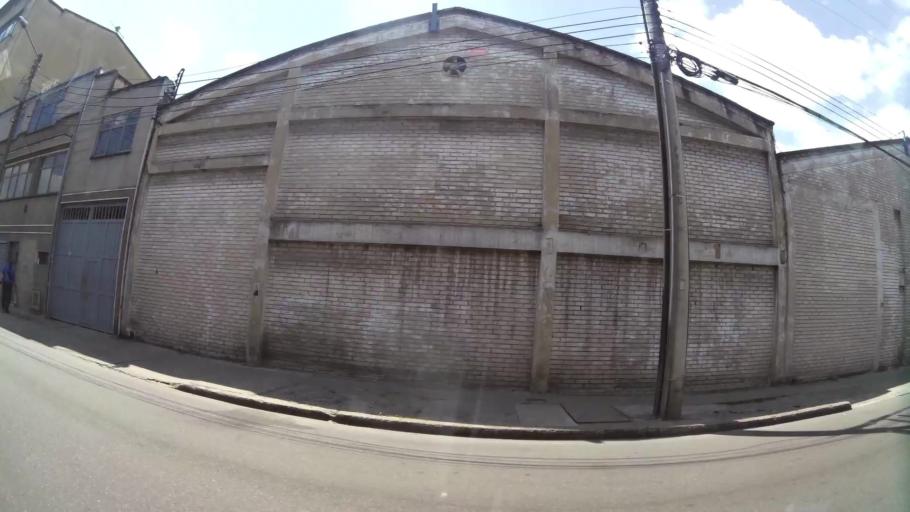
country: CO
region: Bogota D.C.
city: Bogota
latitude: 4.6276
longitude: -74.0991
